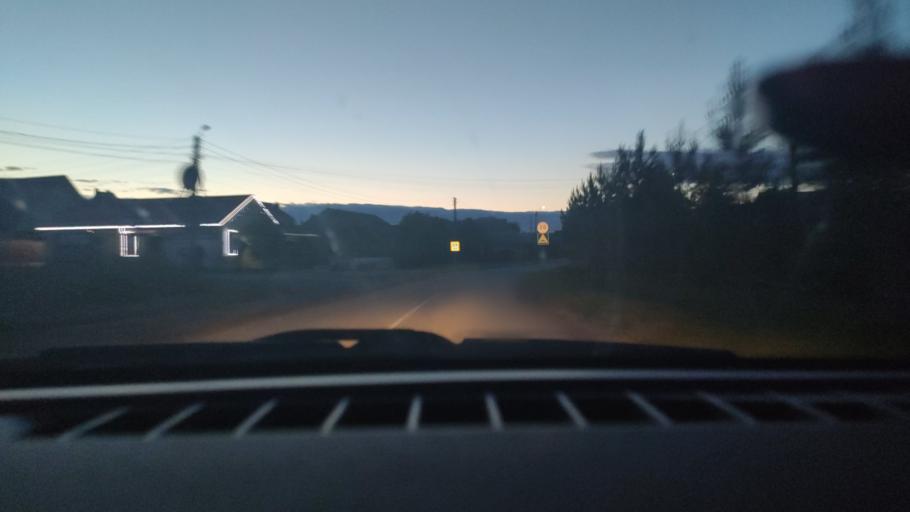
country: RU
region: Perm
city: Polazna
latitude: 58.2787
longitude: 56.4074
